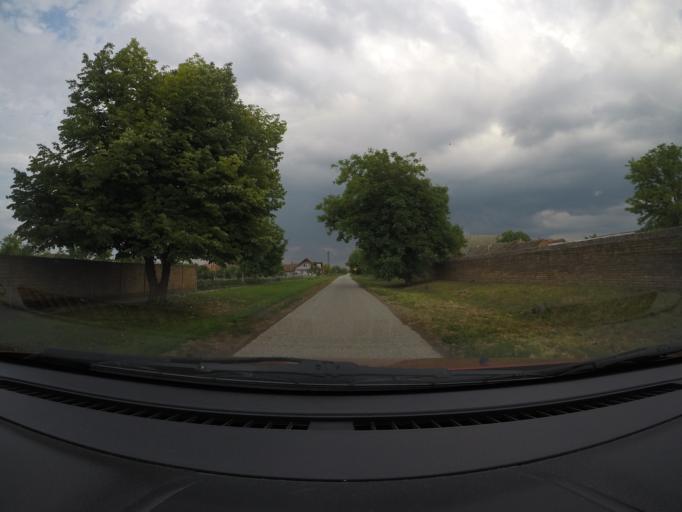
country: RS
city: Uzdin
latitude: 45.2021
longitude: 20.6170
